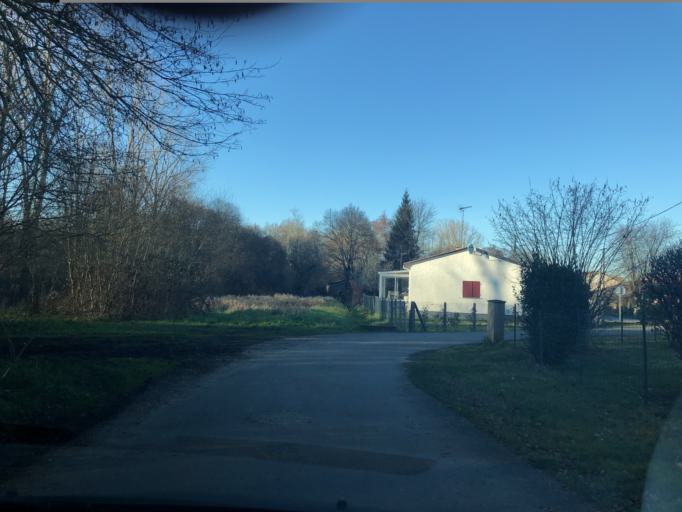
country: FR
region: Aquitaine
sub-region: Departement de la Gironde
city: Avensan
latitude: 45.0388
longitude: -0.7686
